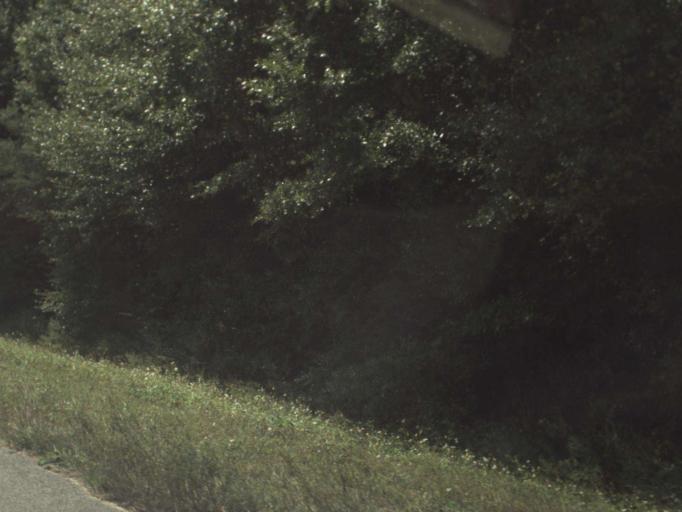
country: US
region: Florida
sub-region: Bay County
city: Youngstown
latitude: 30.5114
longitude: -85.6582
